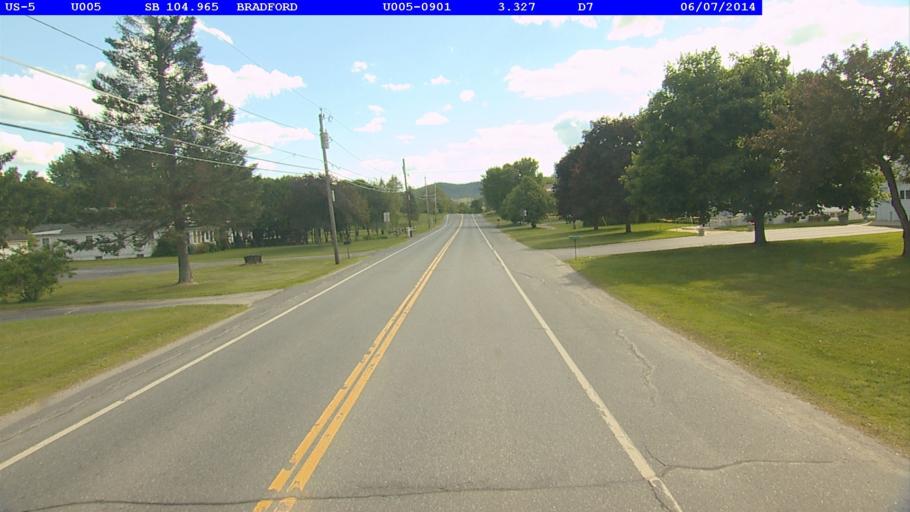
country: US
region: New Hampshire
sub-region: Grafton County
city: Haverhill
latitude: 44.0029
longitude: -72.1164
